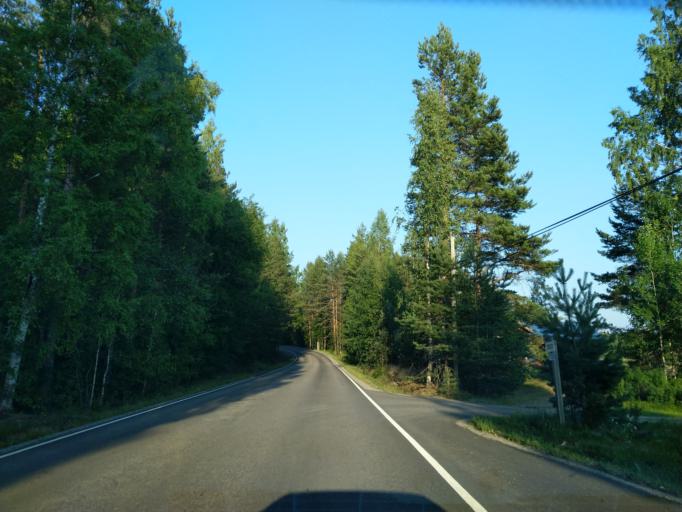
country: FI
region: Satakunta
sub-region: Pohjois-Satakunta
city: Honkajoki
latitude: 61.8200
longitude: 22.2221
